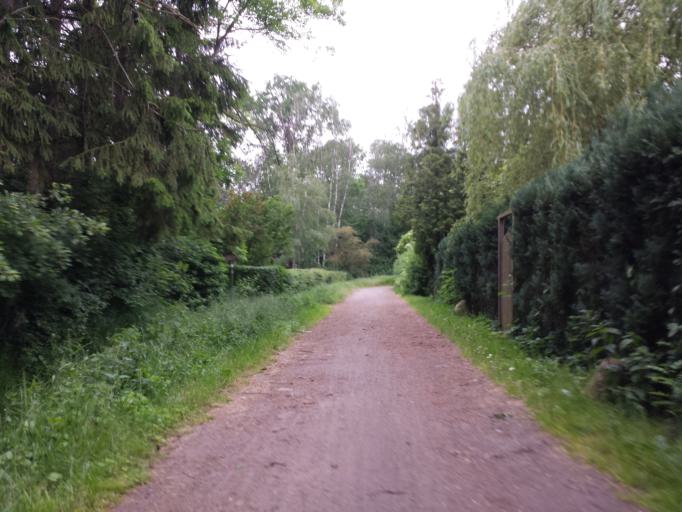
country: DE
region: Bremen
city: Bremen
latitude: 53.1106
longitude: 8.8114
